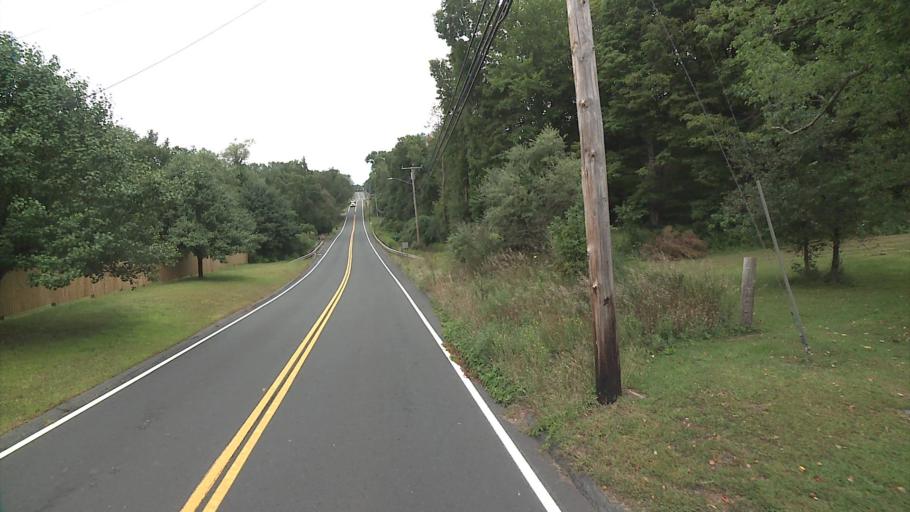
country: US
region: Connecticut
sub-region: Tolland County
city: Rockville
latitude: 41.8266
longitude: -72.4638
